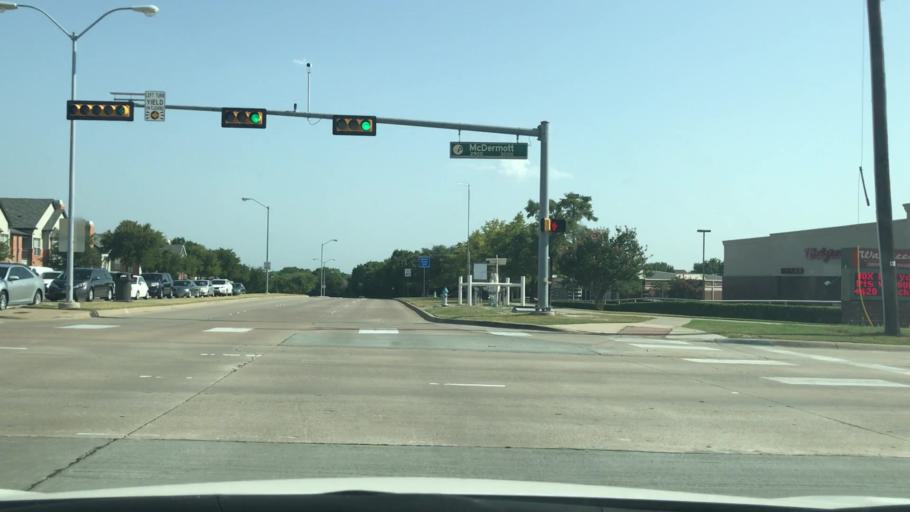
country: US
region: Texas
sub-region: Collin County
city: Allen
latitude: 33.1009
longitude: -96.7503
